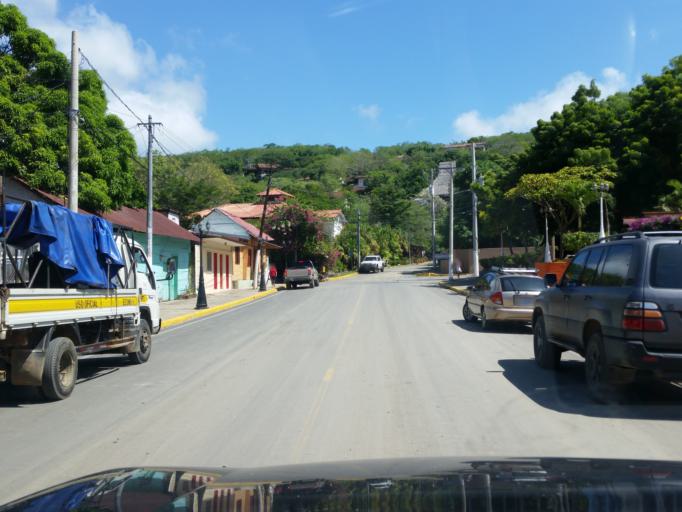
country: NI
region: Rivas
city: San Juan del Sur
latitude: 11.2527
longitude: -85.8700
